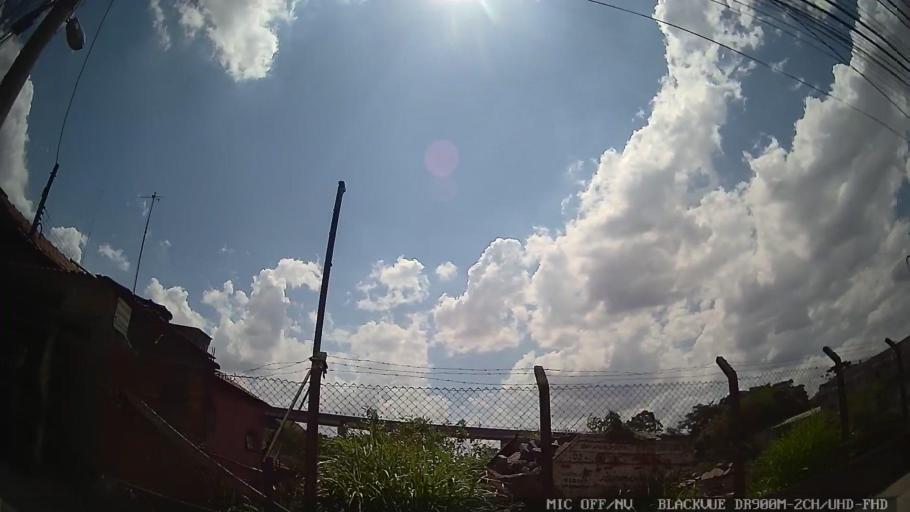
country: BR
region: Sao Paulo
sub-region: Ferraz De Vasconcelos
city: Ferraz de Vasconcelos
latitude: -23.5448
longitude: -46.4608
